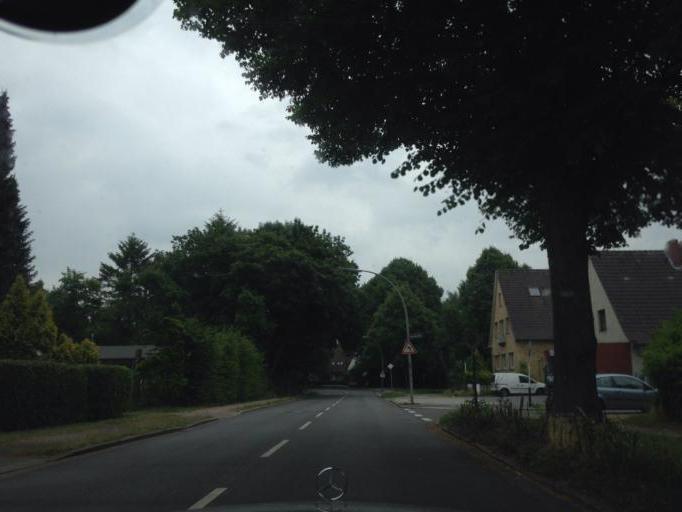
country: DE
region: Hamburg
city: Wandsbek
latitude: 53.5741
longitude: 10.1180
